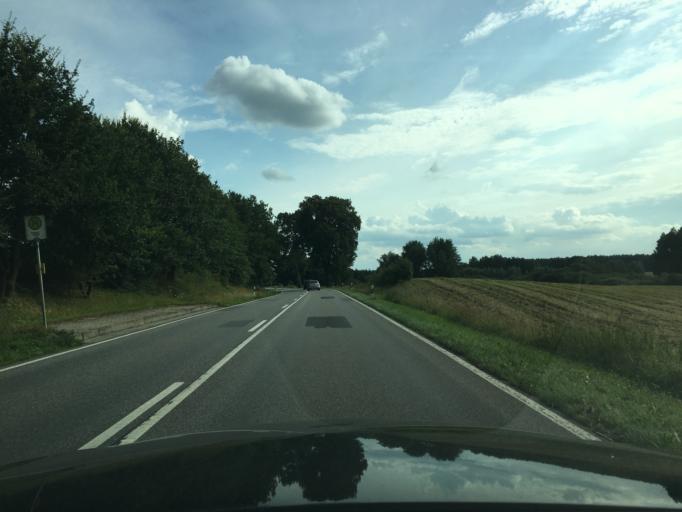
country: DE
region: Mecklenburg-Vorpommern
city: Penzlin
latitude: 53.4354
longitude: 13.0481
